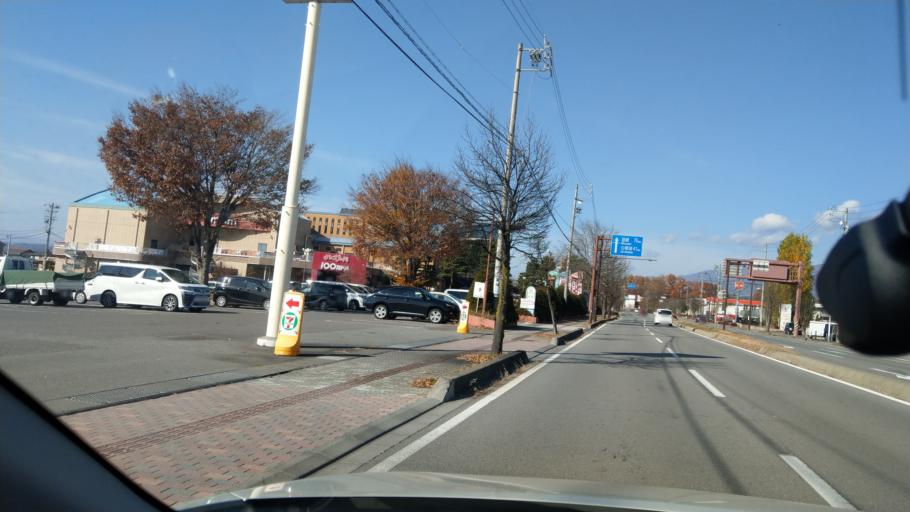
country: JP
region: Nagano
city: Komoro
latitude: 36.2860
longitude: 138.4797
